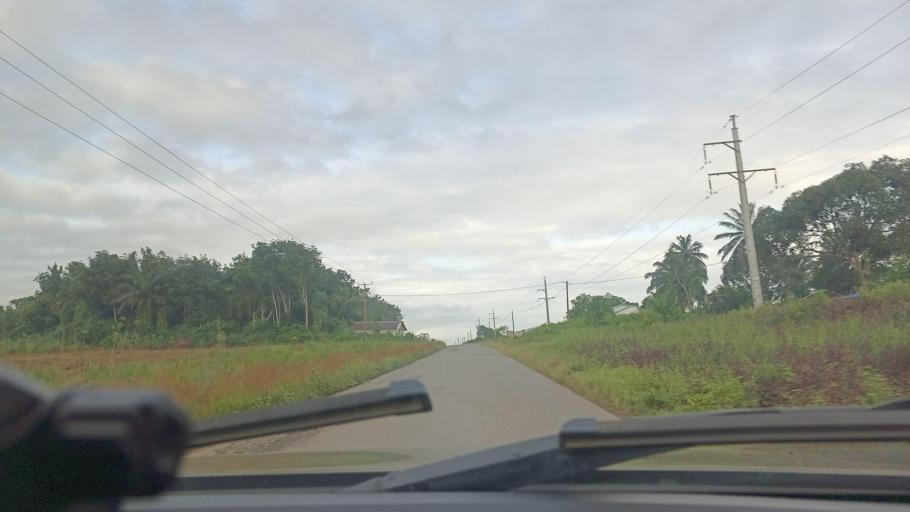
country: LR
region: Montserrado
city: Monrovia
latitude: 6.5684
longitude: -10.8757
